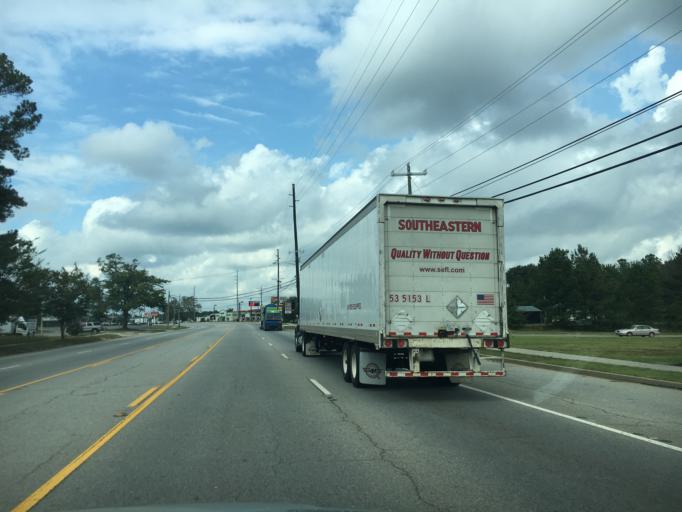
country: US
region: Georgia
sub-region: Elbert County
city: Elberton
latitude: 34.0972
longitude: -82.8475
